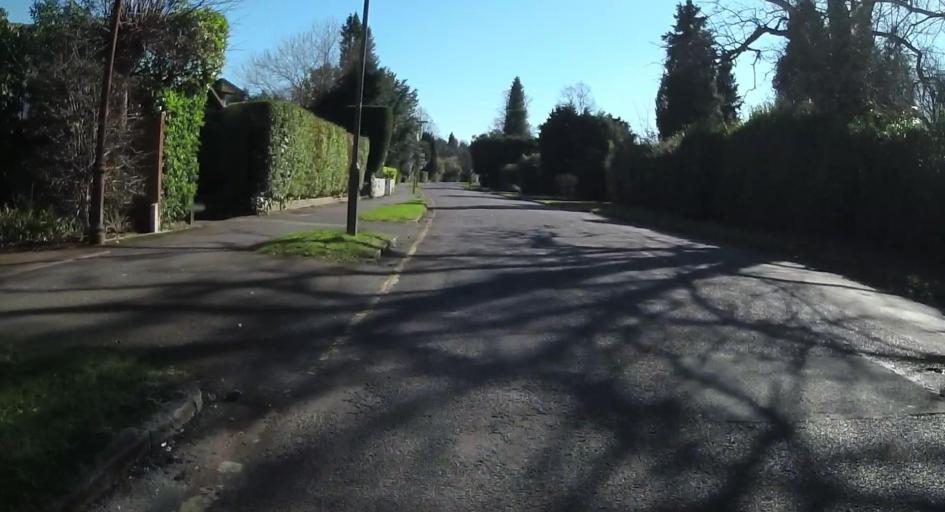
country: GB
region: England
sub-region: Surrey
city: Walton-on-Thames
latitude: 51.3790
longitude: -0.4184
